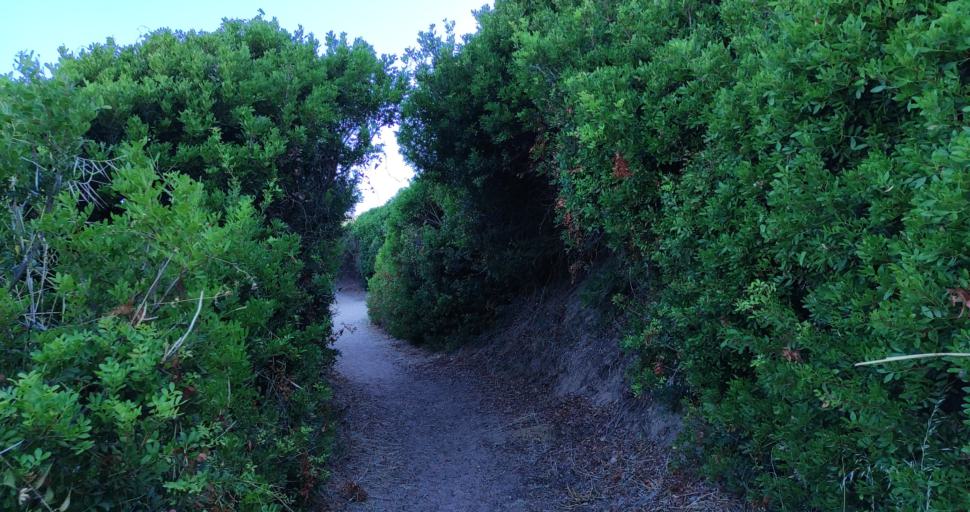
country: FR
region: Corsica
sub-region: Departement de la Corse-du-Sud
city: Alata
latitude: 41.9836
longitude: 8.6698
